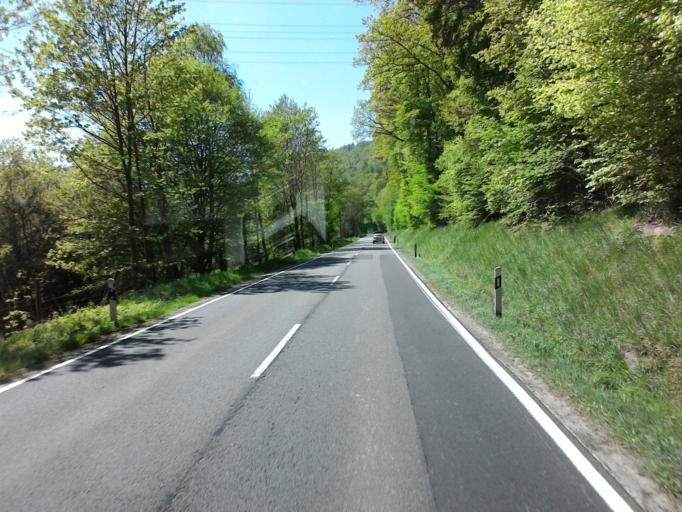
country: DE
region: Bavaria
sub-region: Regierungsbezirk Unterfranken
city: Lohr am Main
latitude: 49.9822
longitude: 9.5426
